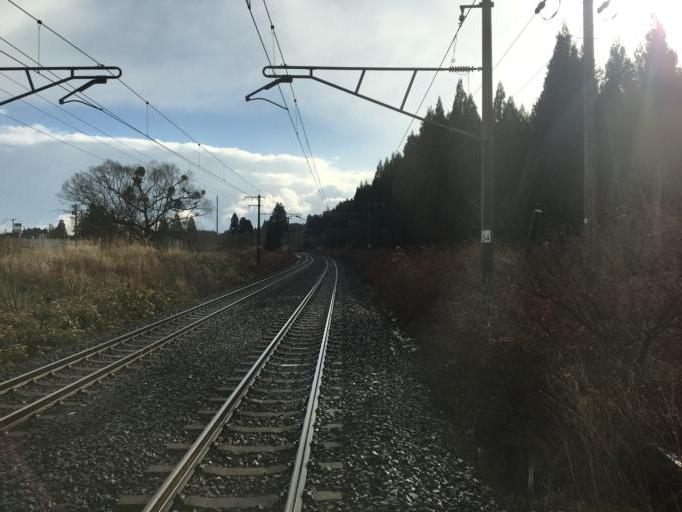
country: JP
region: Aomori
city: Aomori Shi
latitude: 40.9151
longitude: 141.0366
